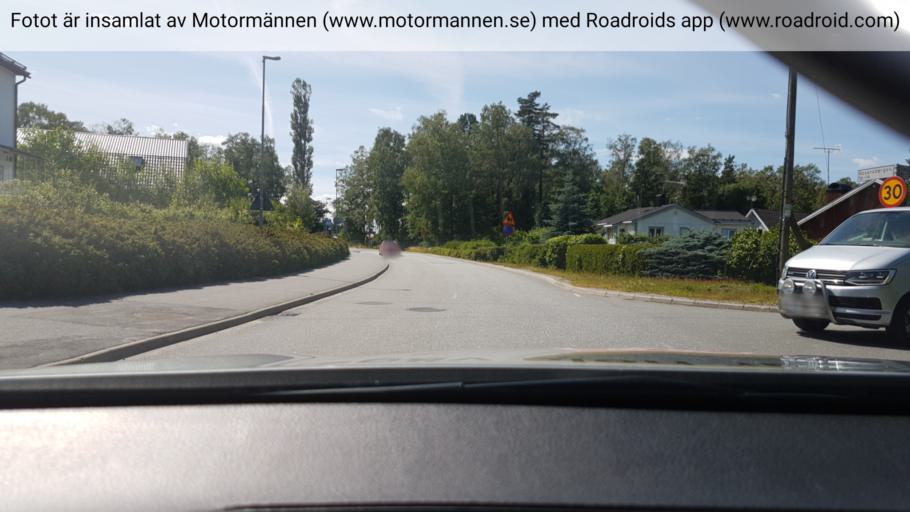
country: SE
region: Stockholm
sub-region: Sigtuna Kommun
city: Rosersberg
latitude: 59.5837
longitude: 17.8931
